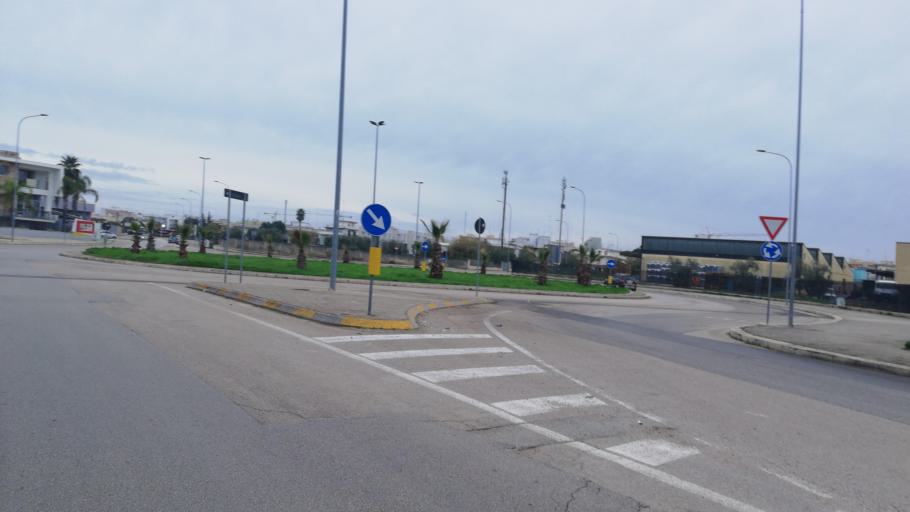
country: IT
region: Apulia
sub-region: Provincia di Bari
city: Bitonto
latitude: 41.1167
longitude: 16.6821
